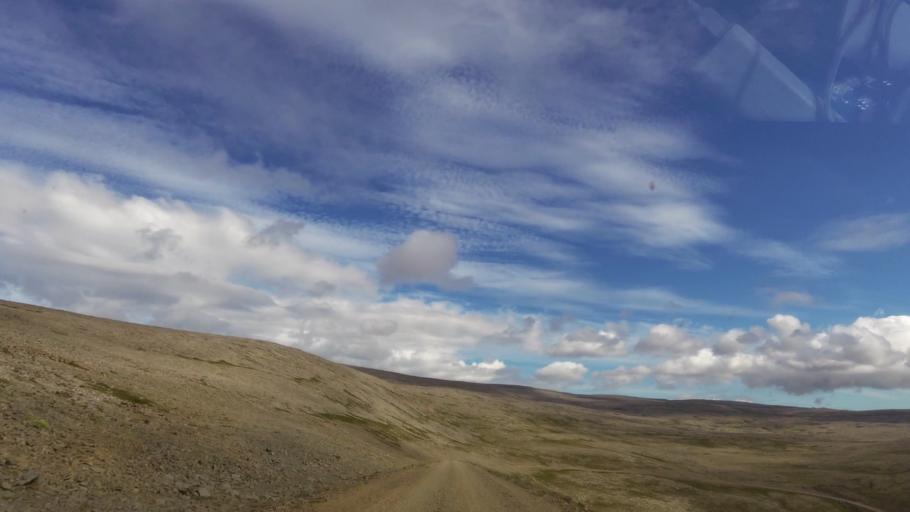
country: IS
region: West
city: Olafsvik
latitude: 65.6181
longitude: -24.3123
